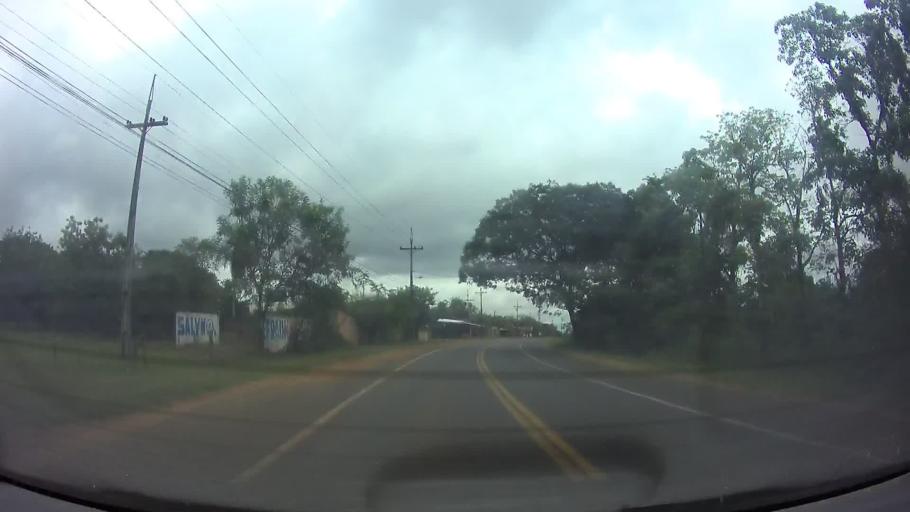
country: PY
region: Central
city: Guarambare
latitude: -25.5013
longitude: -57.4952
